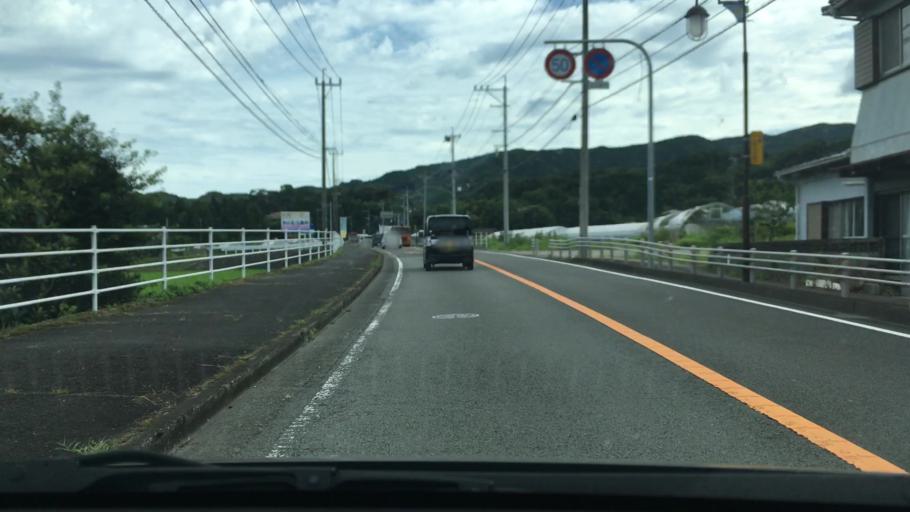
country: JP
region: Nagasaki
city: Togitsu
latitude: 32.9060
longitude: 129.7811
